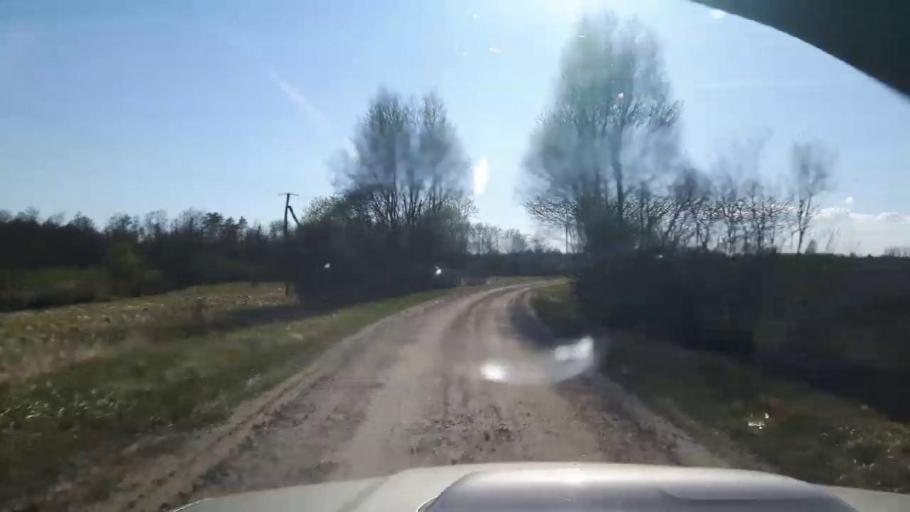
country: EE
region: Paernumaa
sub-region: Tootsi vald
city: Tootsi
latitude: 58.4136
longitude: 24.8496
